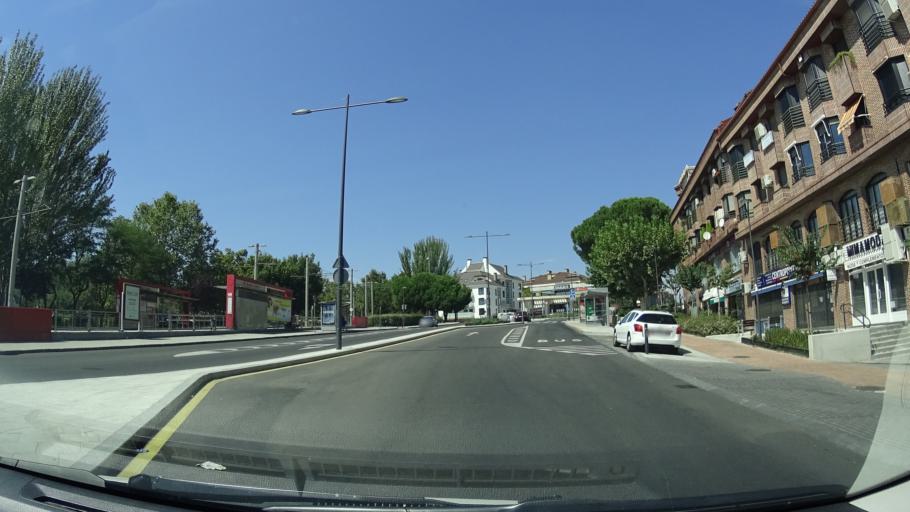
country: ES
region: Madrid
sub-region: Provincia de Madrid
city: Boadilla del Monte
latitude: 40.4073
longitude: -3.8796
